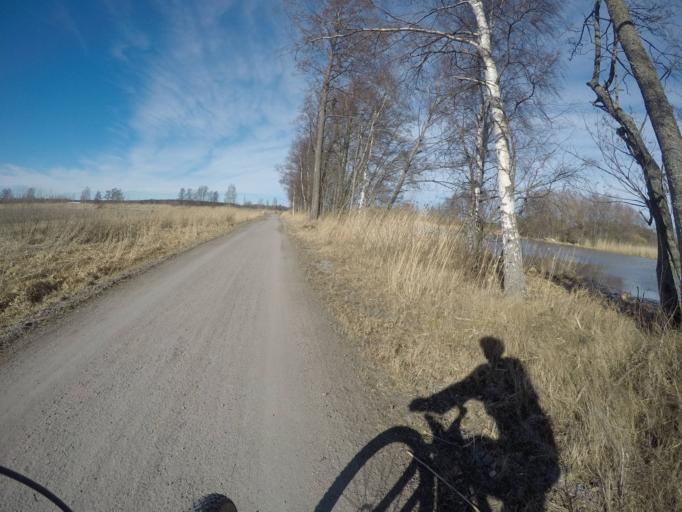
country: SE
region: Soedermanland
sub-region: Eskilstuna Kommun
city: Torshalla
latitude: 59.3985
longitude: 16.4642
